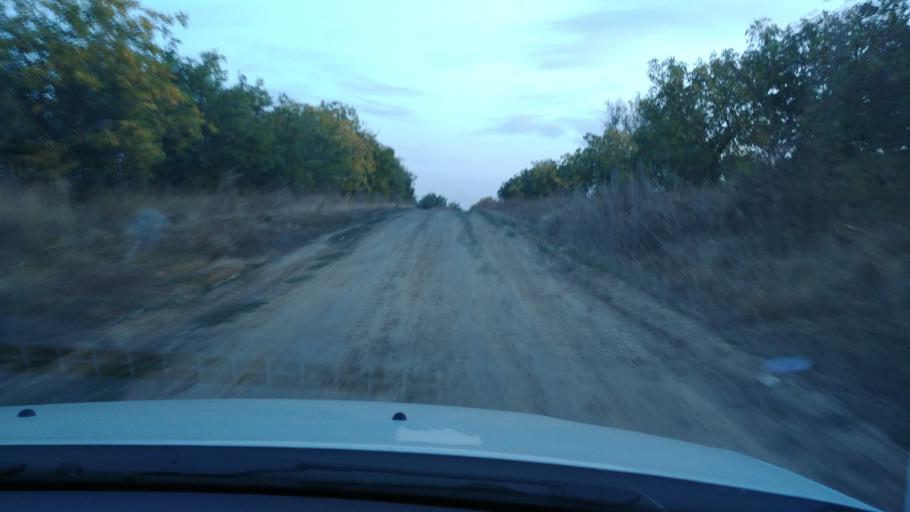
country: MD
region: Rezina
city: Saharna
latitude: 47.6830
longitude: 28.9078
